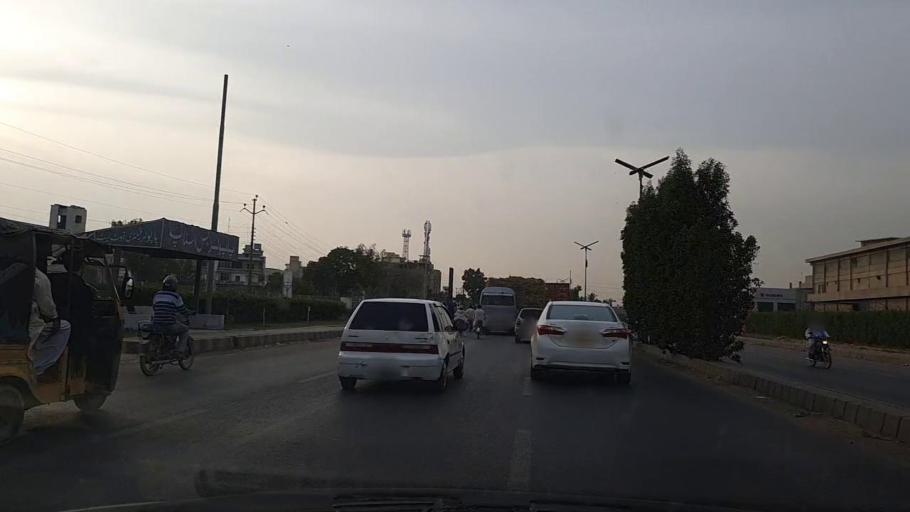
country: PK
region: Sindh
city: Malir Cantonment
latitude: 24.8535
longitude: 67.2463
